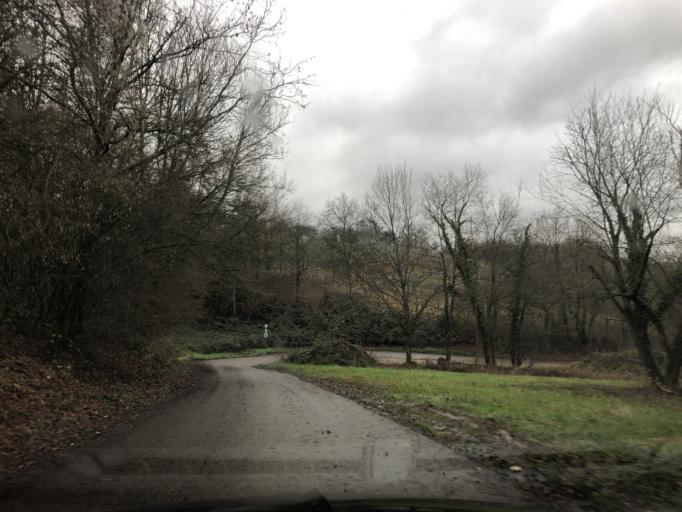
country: DE
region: Baden-Wuerttemberg
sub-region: Karlsruhe Region
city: Bammental
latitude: 49.3433
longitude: 8.7646
